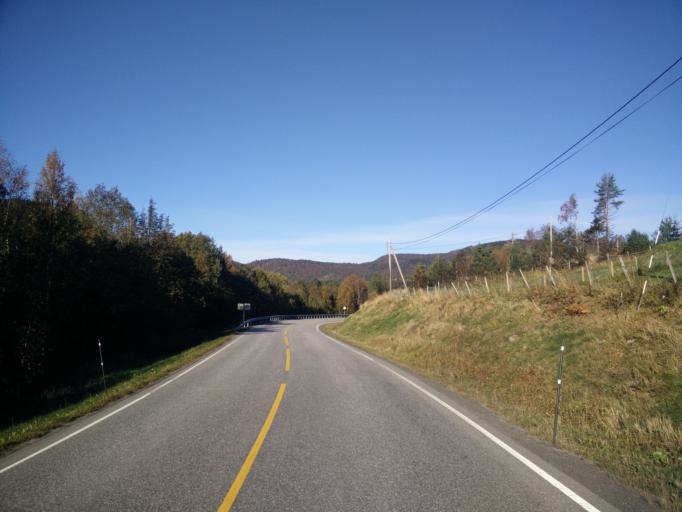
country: NO
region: More og Romsdal
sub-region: Tingvoll
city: Tingvoll
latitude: 63.0406
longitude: 8.0470
